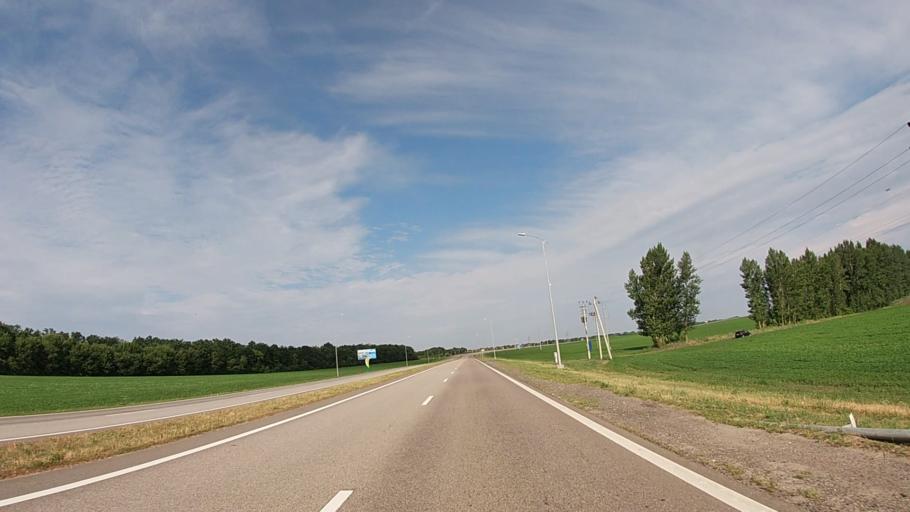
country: RU
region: Belgorod
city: Rakitnoye
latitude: 50.7903
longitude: 35.8784
